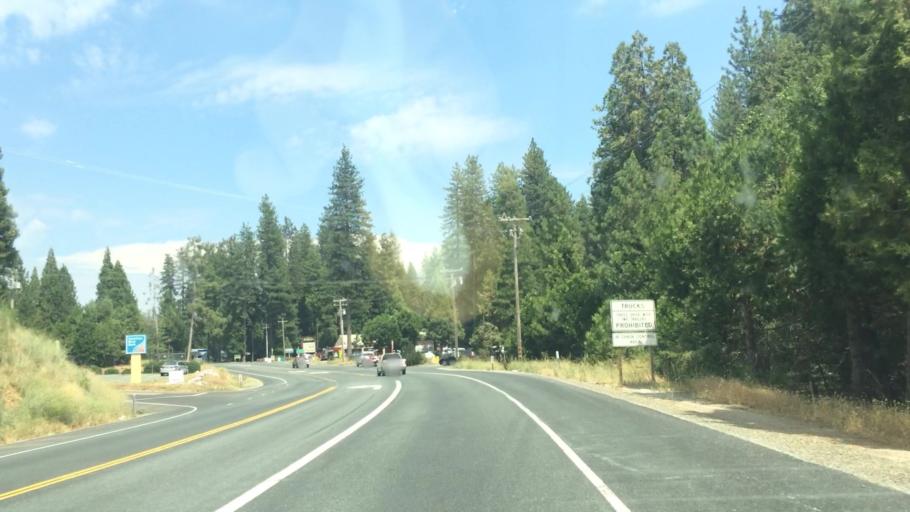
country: US
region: California
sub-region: Amador County
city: Pioneer
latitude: 38.4433
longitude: -120.5366
